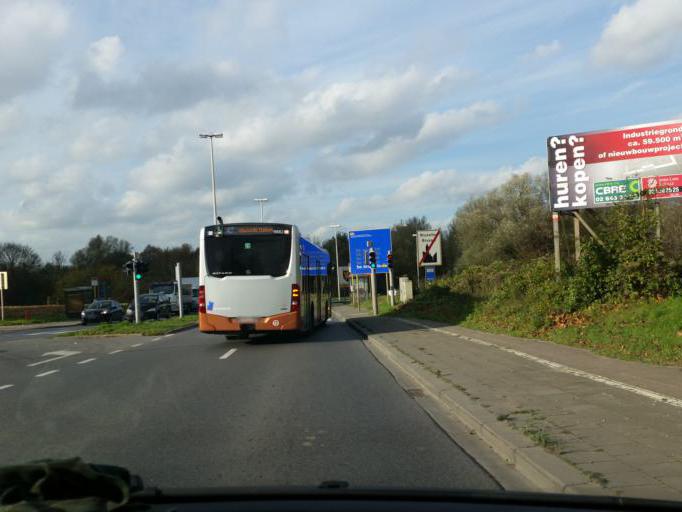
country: BE
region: Flanders
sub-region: Provincie Vlaams-Brabant
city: Grimbergen
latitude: 50.9099
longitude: 4.3916
